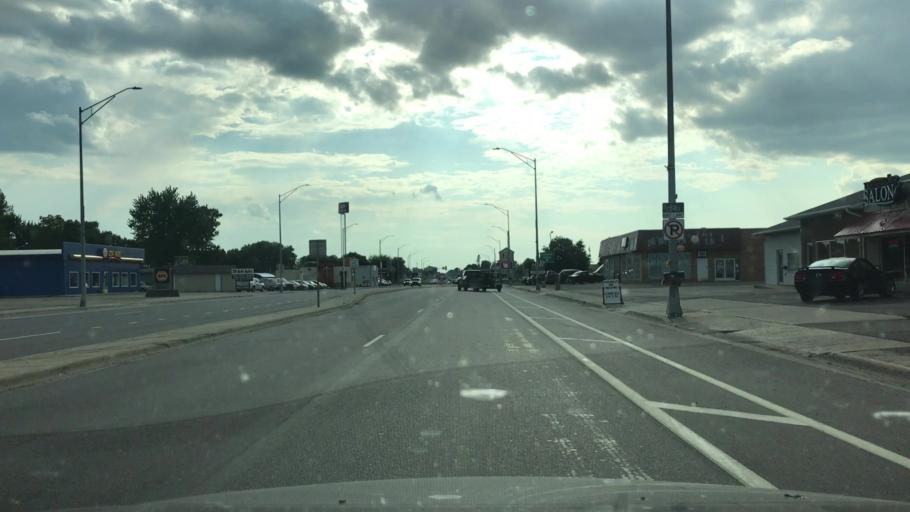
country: US
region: Minnesota
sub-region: Nobles County
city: Worthington
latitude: 43.6314
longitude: -95.5895
